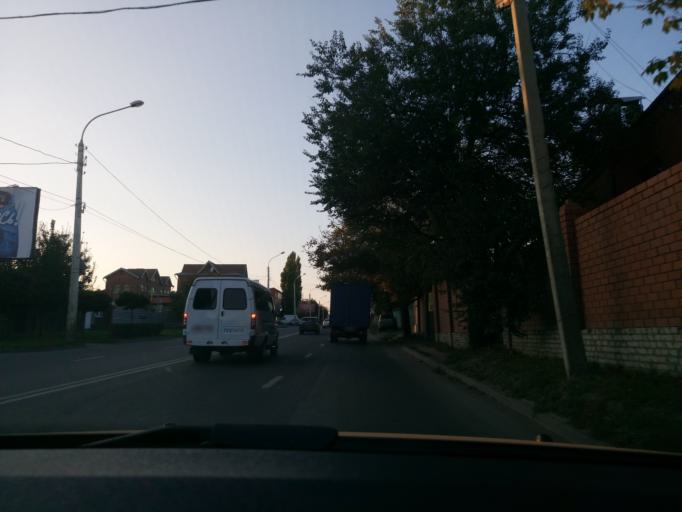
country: RU
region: Rostov
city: Rostov-na-Donu
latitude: 47.2314
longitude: 39.6433
